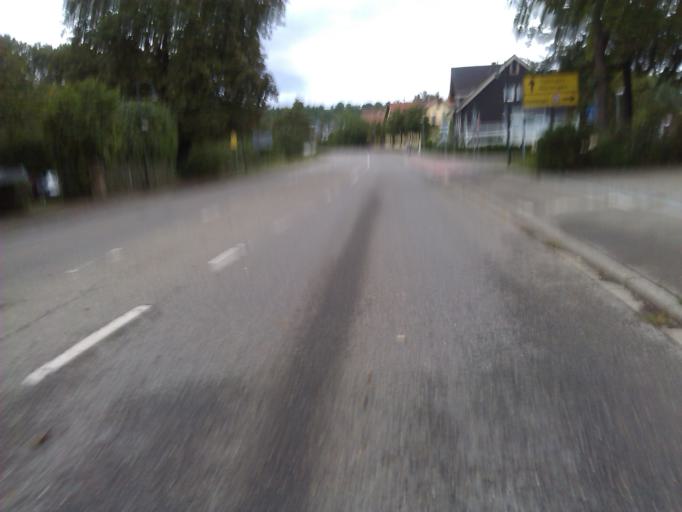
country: DE
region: Baden-Wuerttemberg
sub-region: Regierungsbezirk Stuttgart
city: Neckartailfingen
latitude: 48.6091
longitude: 9.2676
